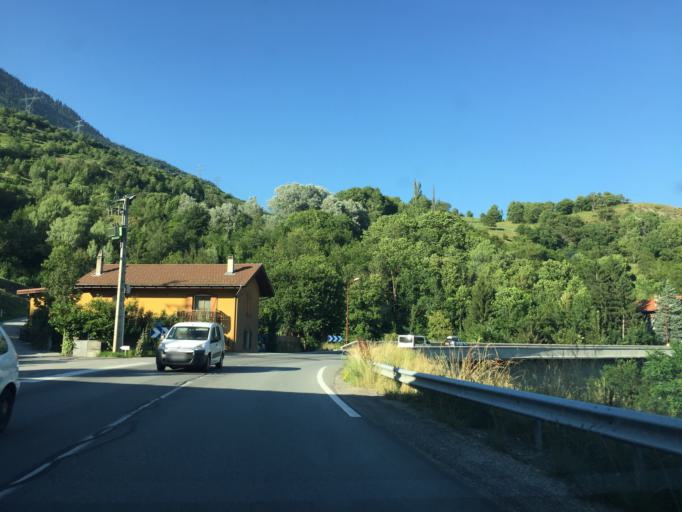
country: FR
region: Rhone-Alpes
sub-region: Departement de la Savoie
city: Aime
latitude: 45.5502
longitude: 6.6190
